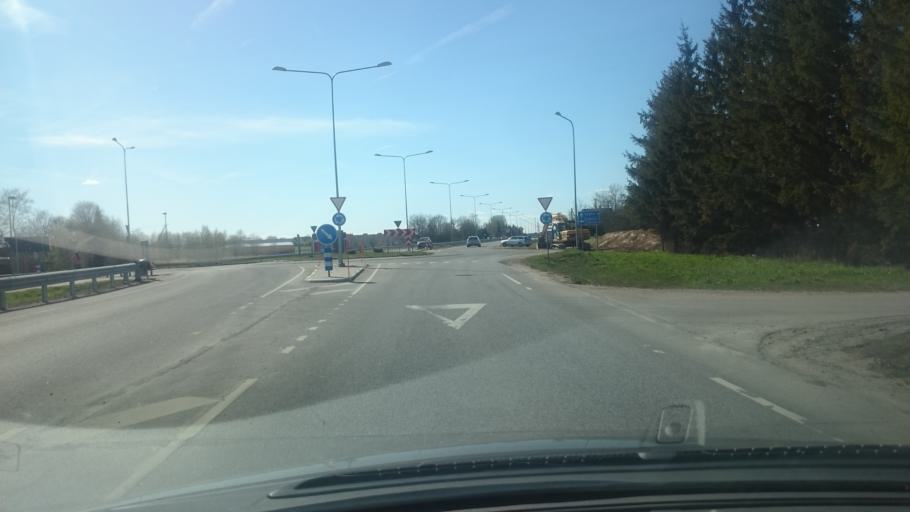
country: EE
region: Tartu
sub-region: Tartu linn
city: Tartu
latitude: 58.3723
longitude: 26.8008
